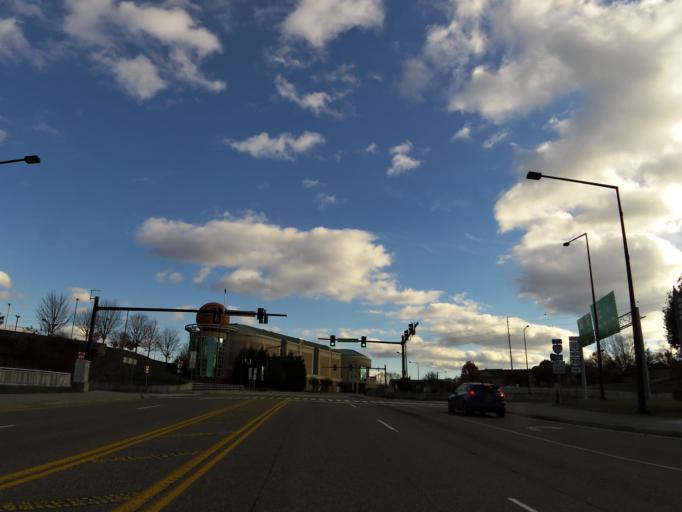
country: US
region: Tennessee
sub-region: Knox County
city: Knoxville
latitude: 35.9644
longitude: -83.9121
